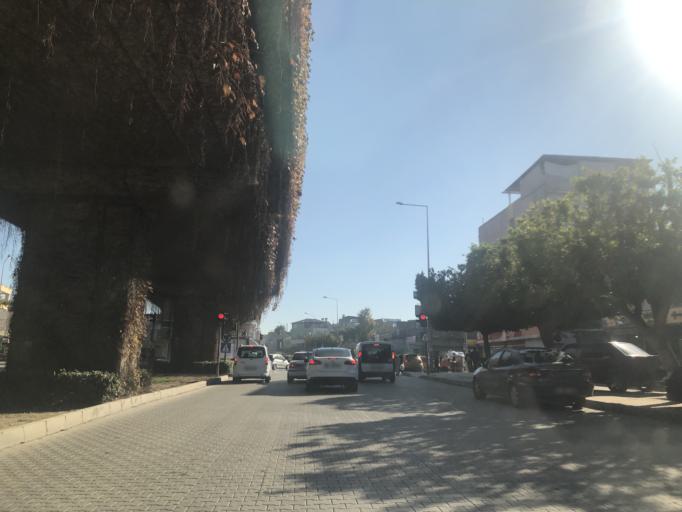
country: TR
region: Adana
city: Seyhan
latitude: 36.9793
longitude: 35.3233
